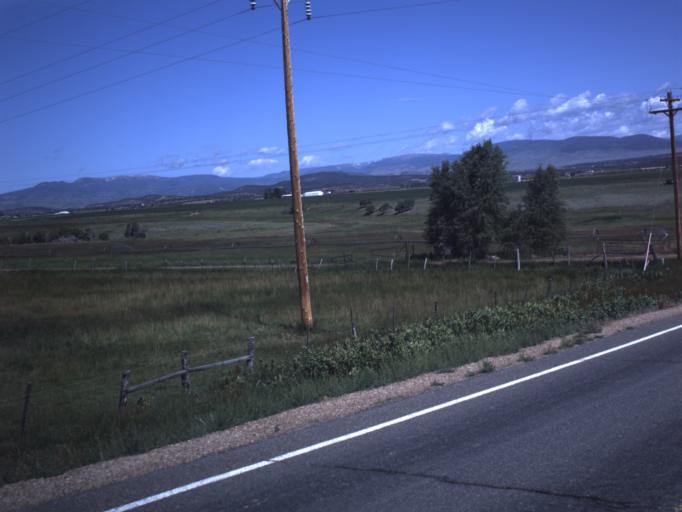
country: US
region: Utah
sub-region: Duchesne County
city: Duchesne
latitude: 40.3321
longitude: -110.4079
